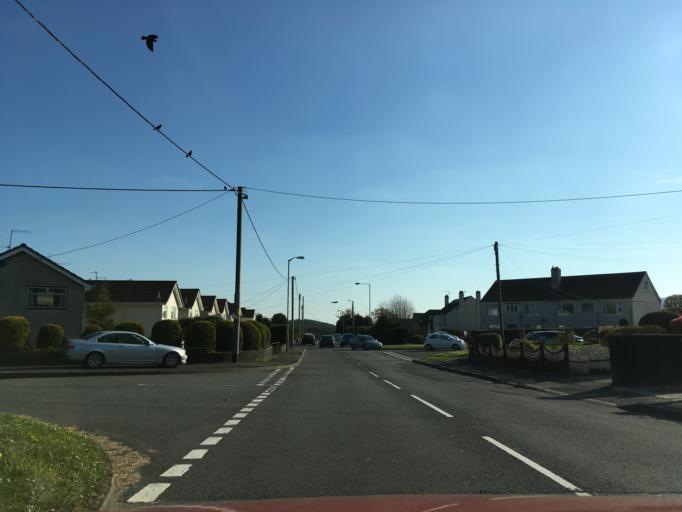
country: GB
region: Wales
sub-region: Torfaen County Borough
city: New Inn
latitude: 51.6887
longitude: -3.0038
